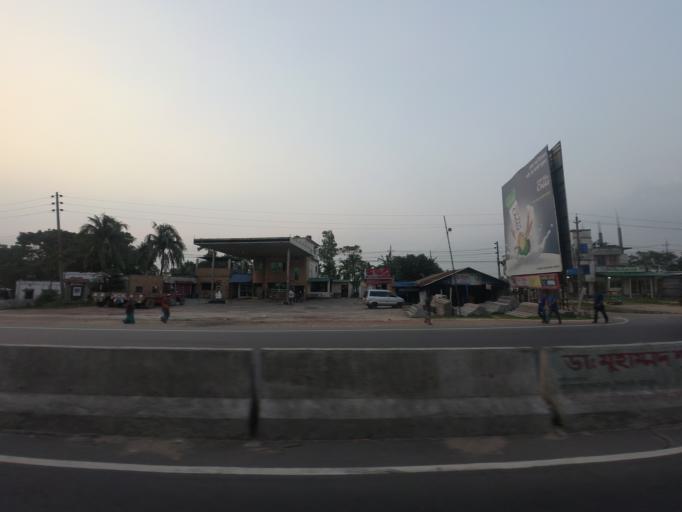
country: BD
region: Chittagong
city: Comilla
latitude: 23.4799
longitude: 91.1269
